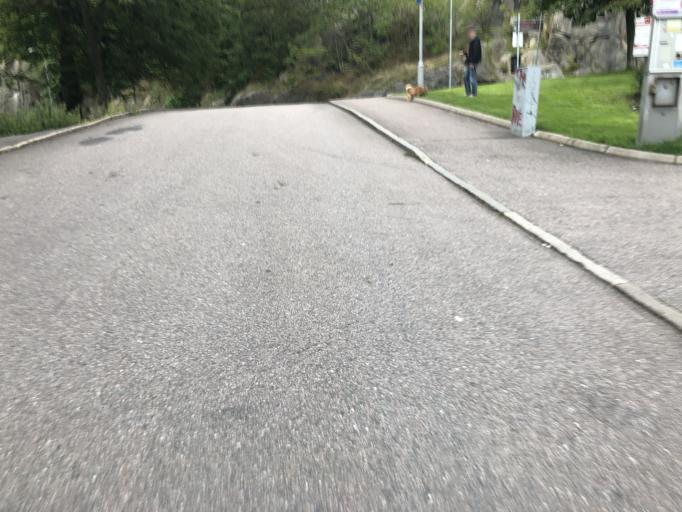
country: SE
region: Vaestra Goetaland
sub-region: Goteborg
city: Majorna
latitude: 57.6921
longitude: 11.9189
